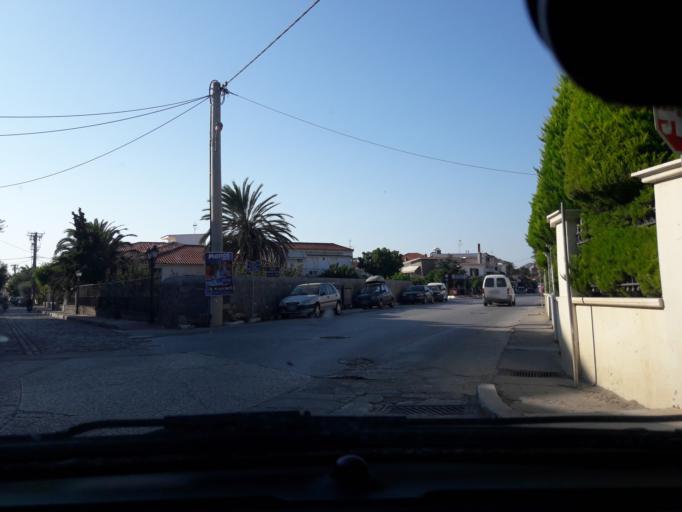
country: GR
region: North Aegean
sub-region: Nomos Lesvou
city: Myrina
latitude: 39.8751
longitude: 25.0636
